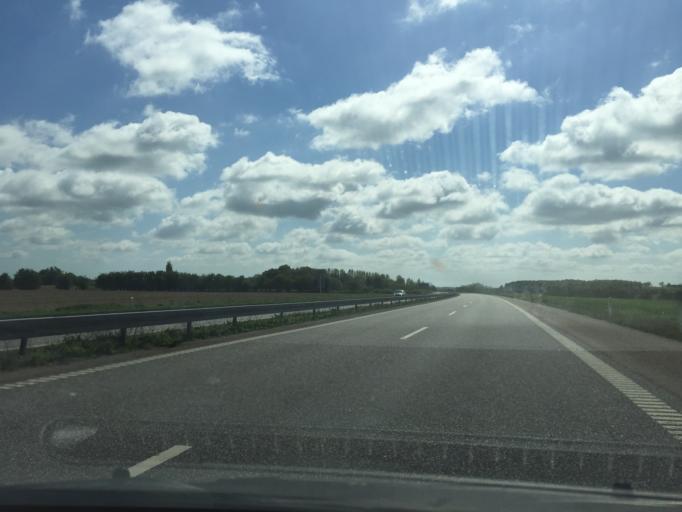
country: DK
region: Zealand
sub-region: Guldborgsund Kommune
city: Sundby
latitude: 54.8546
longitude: 11.8376
